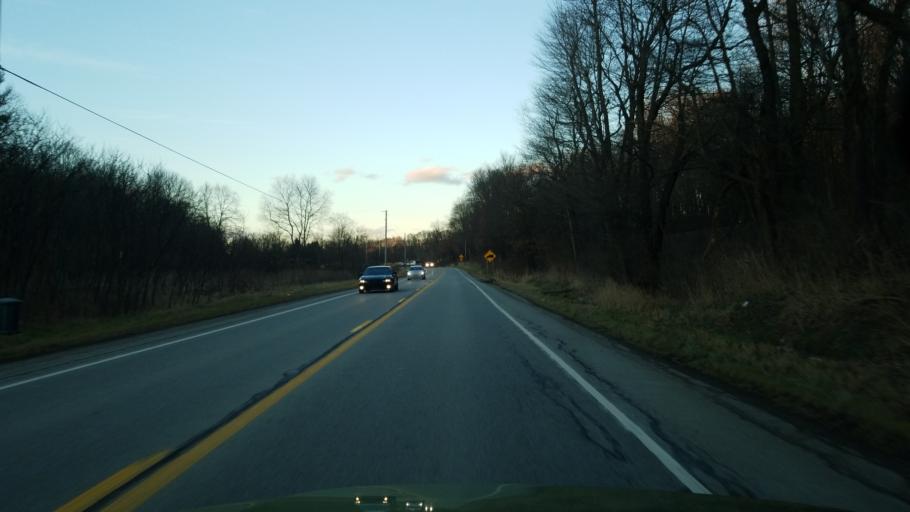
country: US
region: Pennsylvania
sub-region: Indiana County
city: Clymer
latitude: 40.7793
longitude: -79.0544
